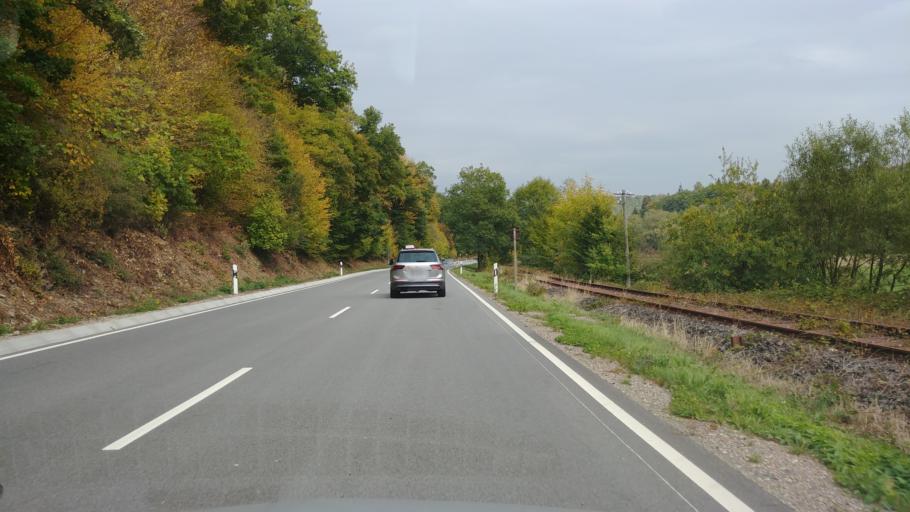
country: DE
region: Rheinland-Pfalz
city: Eisighofen
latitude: 50.2287
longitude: 8.0481
